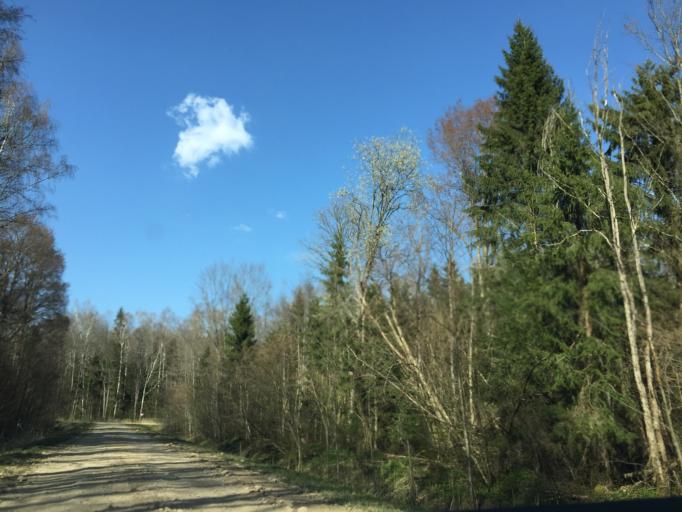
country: LV
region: Lielvarde
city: Lielvarde
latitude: 56.8537
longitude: 24.8040
